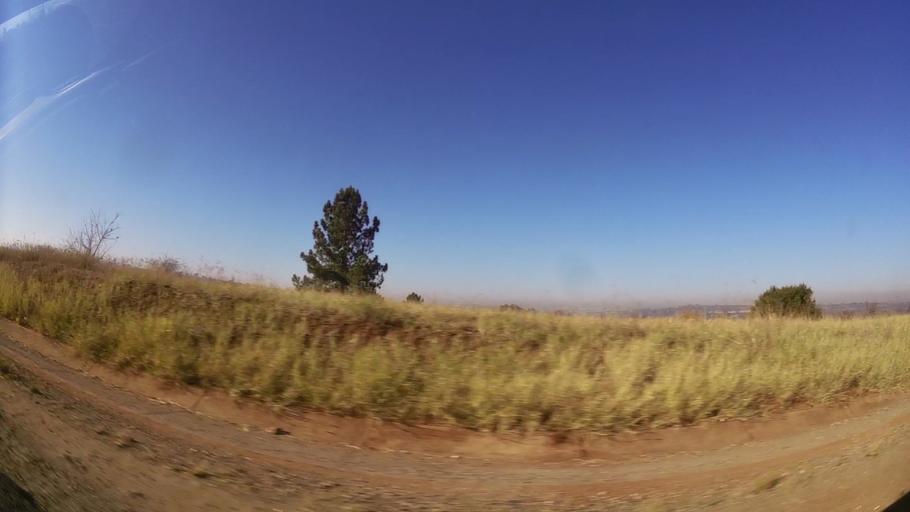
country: ZA
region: Gauteng
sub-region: City of Tshwane Metropolitan Municipality
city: Centurion
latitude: -25.8225
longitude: 28.1680
